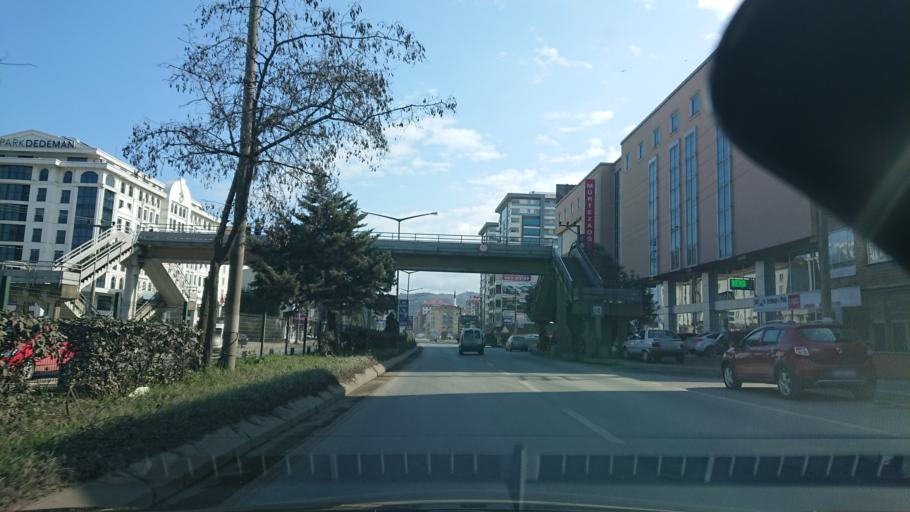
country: TR
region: Trabzon
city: Yomra
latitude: 40.9617
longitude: 39.8422
